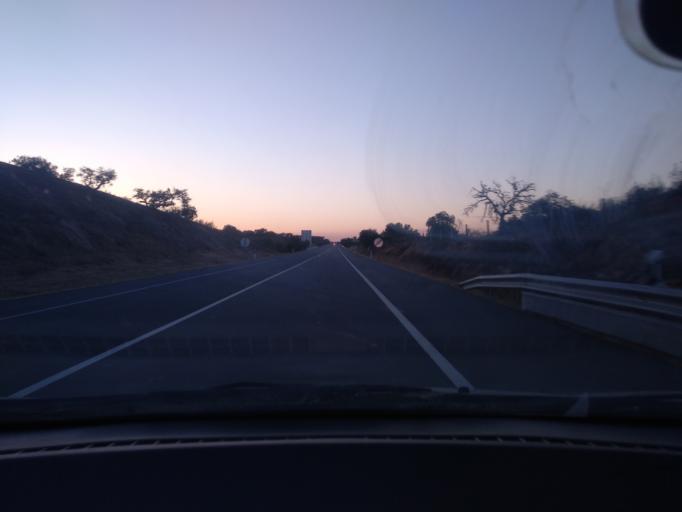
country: PT
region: Beja
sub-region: Beja
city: Beja
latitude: 37.9386
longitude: -7.8725
